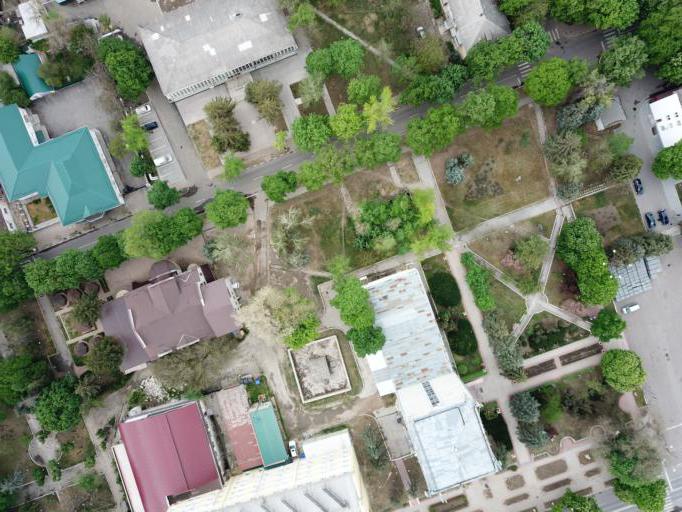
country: MD
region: Ungheni
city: Ungheni
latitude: 47.2056
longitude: 27.7975
